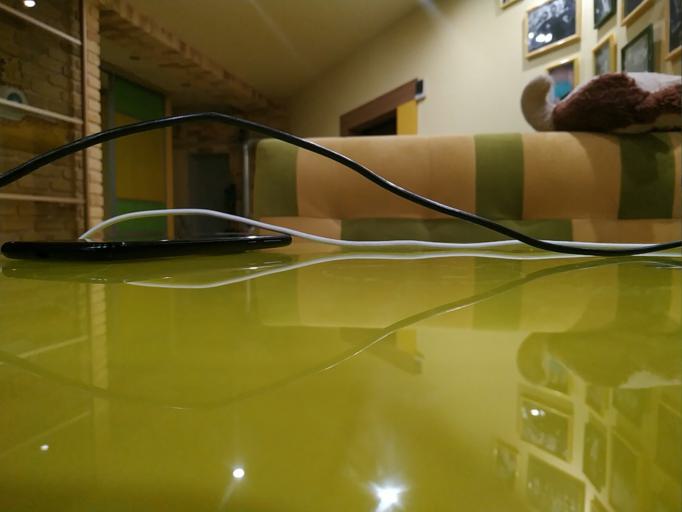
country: RU
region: Moscow
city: Shchukino
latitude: 55.7824
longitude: 37.4400
